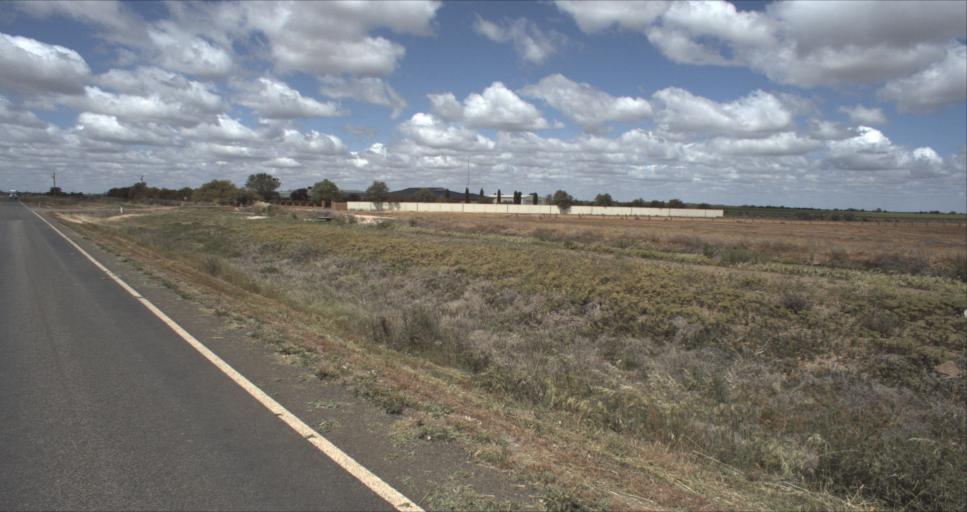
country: AU
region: New South Wales
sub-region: Murrumbidgee Shire
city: Darlington Point
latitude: -34.4854
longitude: 146.1590
